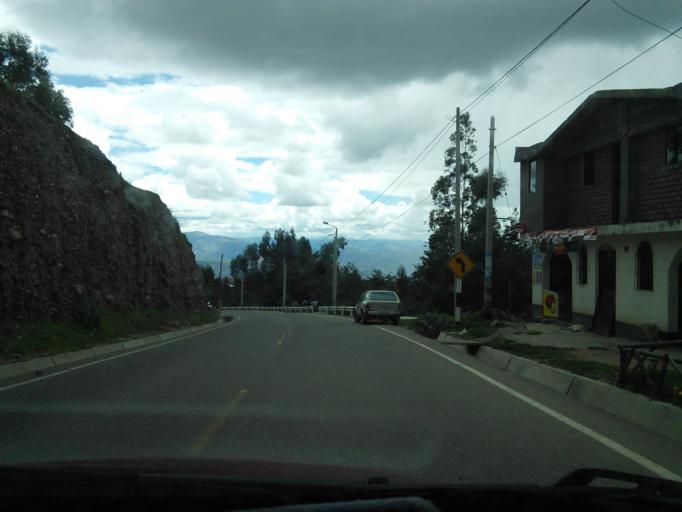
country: PE
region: Ayacucho
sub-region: Provincia de Huamanga
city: Quinua
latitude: -13.0463
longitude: -74.1347
